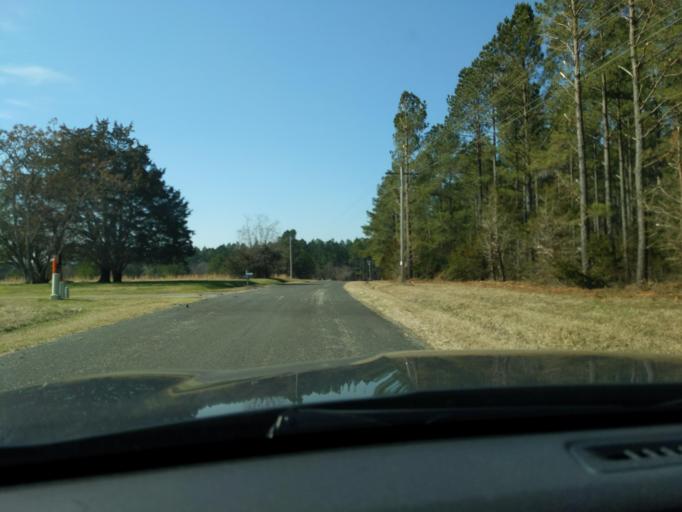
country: US
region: South Carolina
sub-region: Abbeville County
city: Calhoun Falls
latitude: 34.0814
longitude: -82.5685
